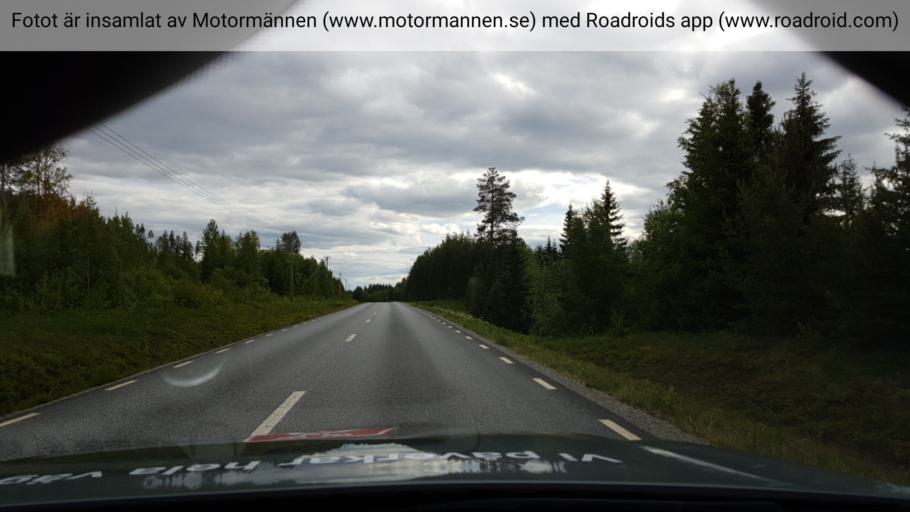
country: SE
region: Jaemtland
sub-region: Stroemsunds Kommun
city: Stroemsund
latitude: 63.9644
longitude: 15.4835
